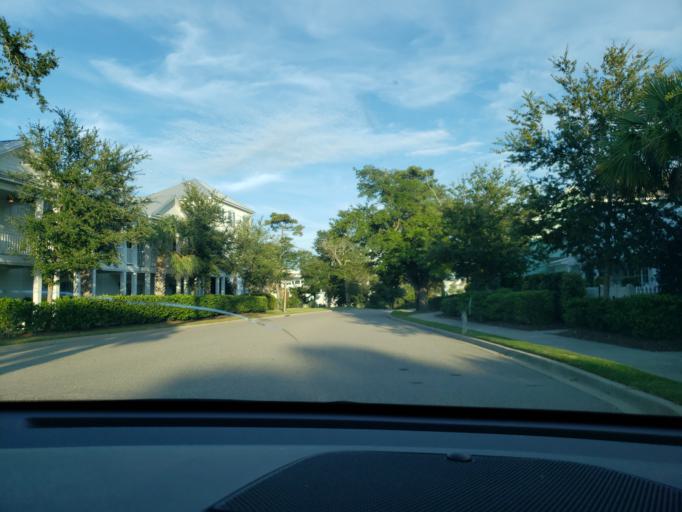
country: US
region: South Carolina
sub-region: Horry County
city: North Myrtle Beach
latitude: 33.7932
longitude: -78.7379
